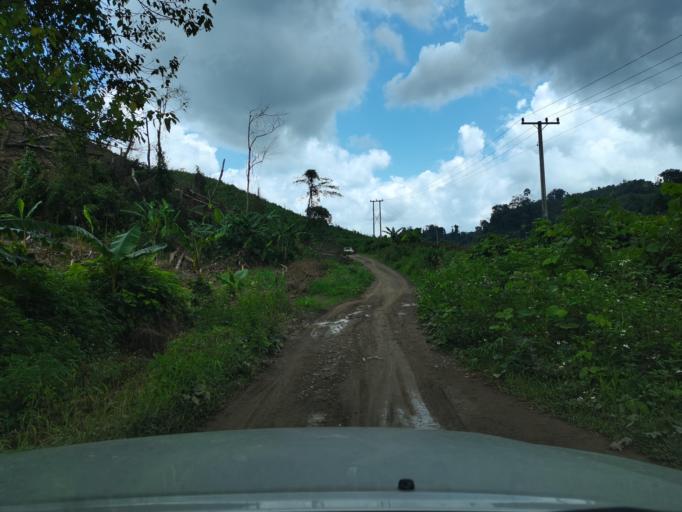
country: LA
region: Loungnamtha
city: Muang Long
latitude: 20.7646
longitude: 101.0177
